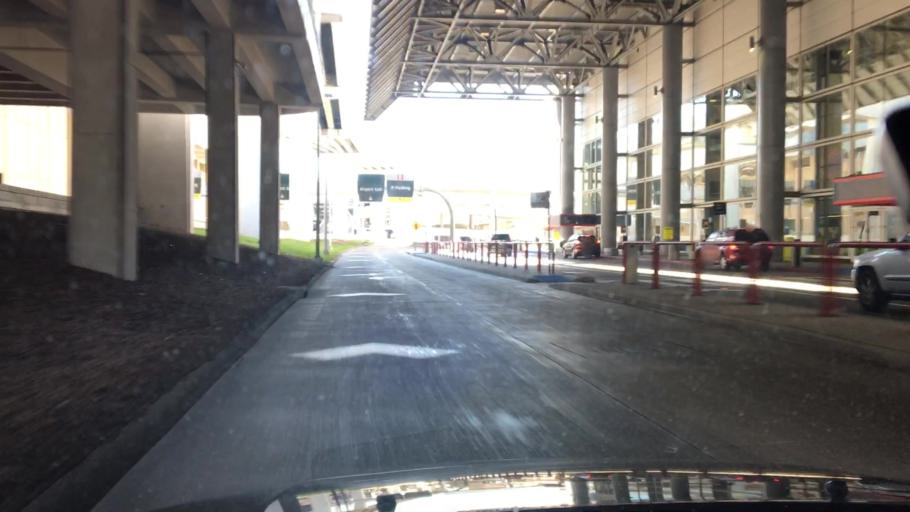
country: US
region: Texas
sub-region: Harris County
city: Aldine
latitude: 29.9873
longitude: -95.3343
